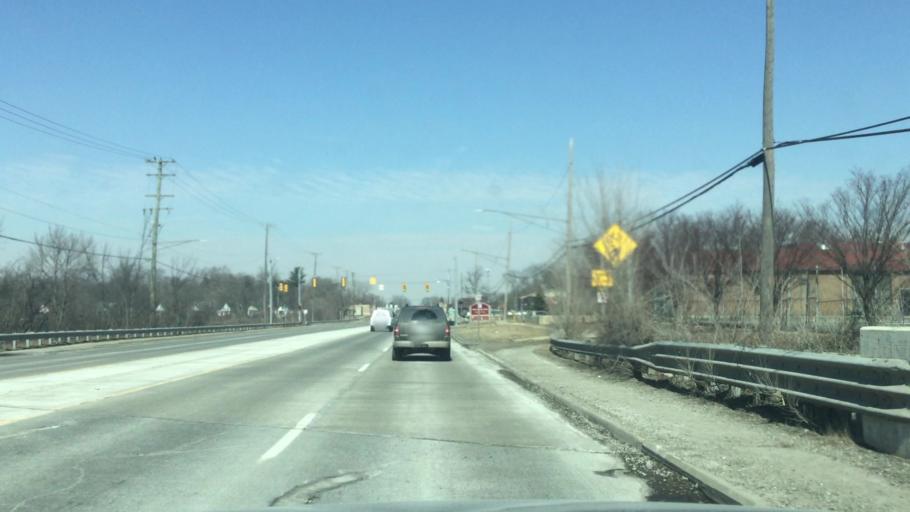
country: US
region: Michigan
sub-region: Wayne County
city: Inkster
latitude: 42.2974
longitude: -83.3101
